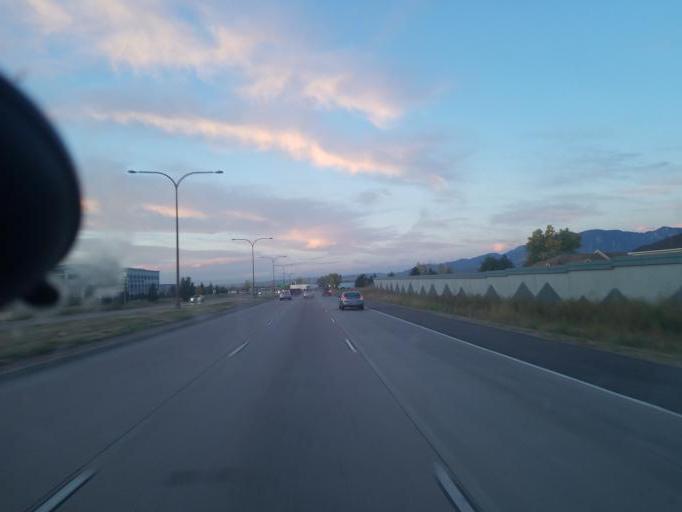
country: US
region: Colorado
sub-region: El Paso County
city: Cimarron Hills
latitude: 38.8199
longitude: -104.7279
